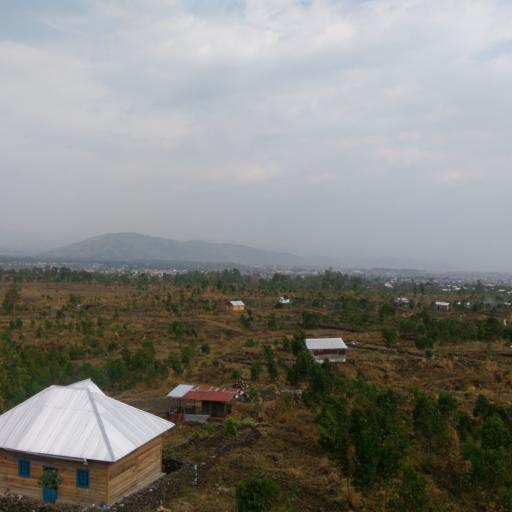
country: CD
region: Nord Kivu
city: Goma
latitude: -1.6309
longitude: 29.2242
